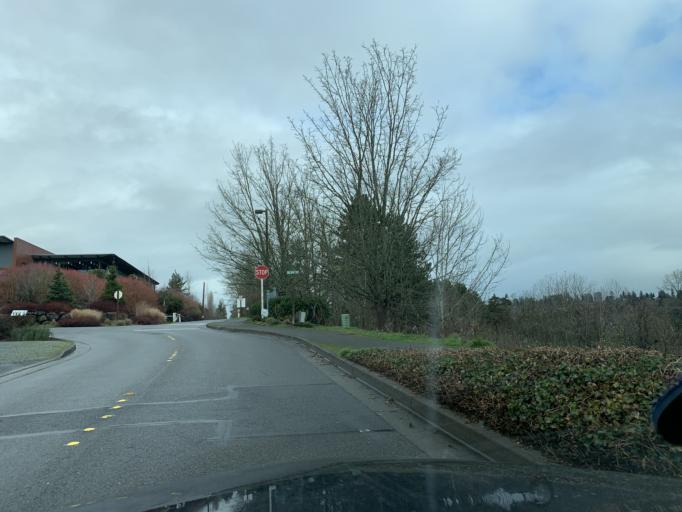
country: US
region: Washington
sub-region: King County
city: Mercer Island
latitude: 47.5887
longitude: -122.2268
